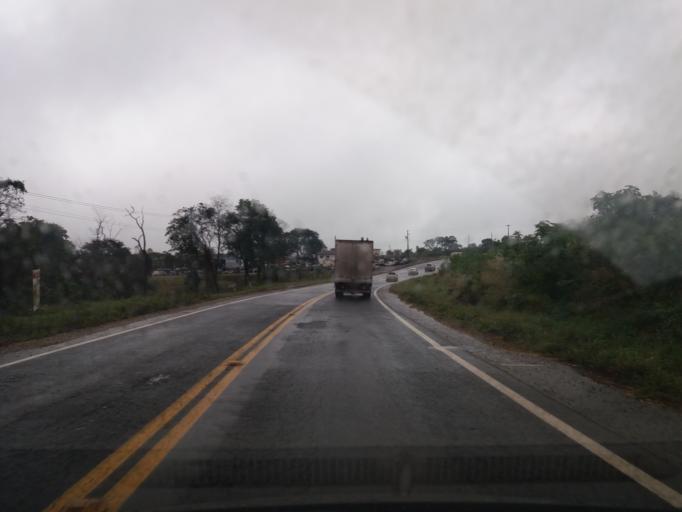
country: BR
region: Parana
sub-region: Realeza
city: Realeza
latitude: -25.4853
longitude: -53.5932
